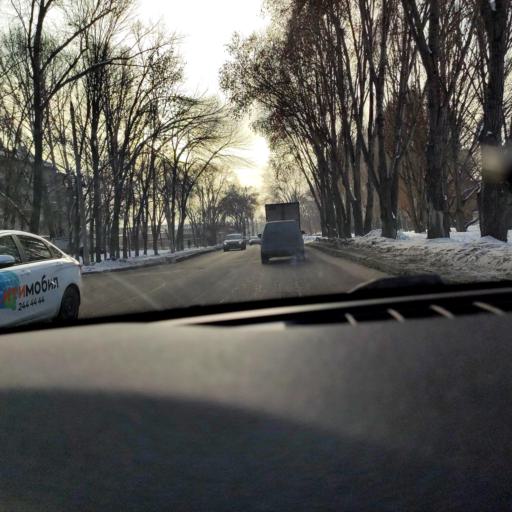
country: RU
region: Samara
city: Petra-Dubrava
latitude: 53.2314
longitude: 50.2923
